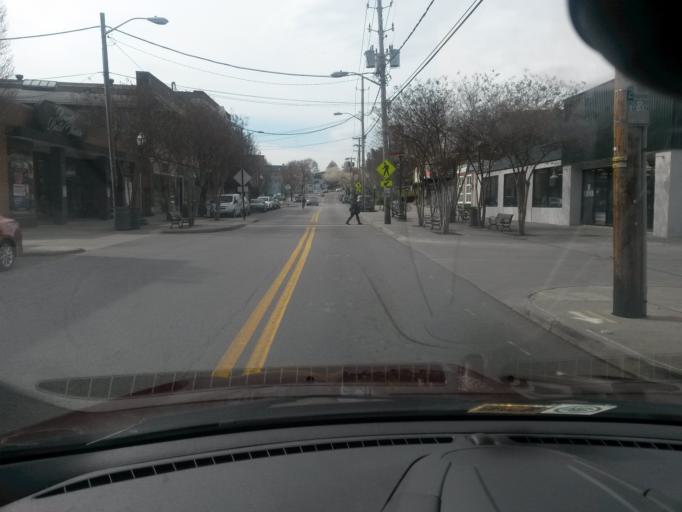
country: US
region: Virginia
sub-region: City of Roanoke
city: Roanoke
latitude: 37.2654
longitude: -79.9771
